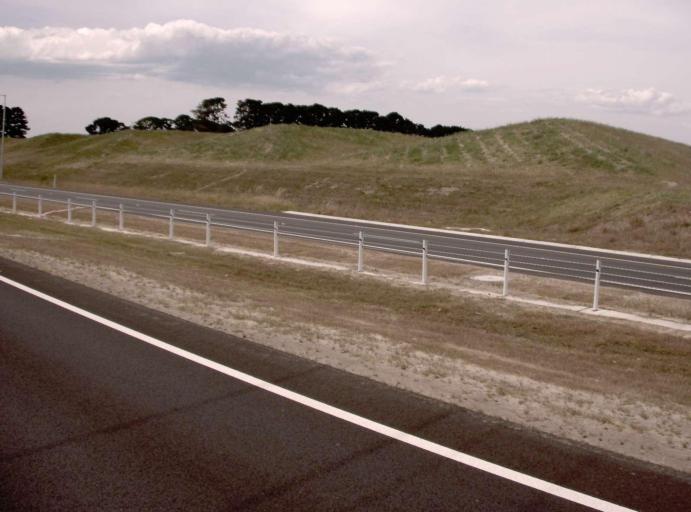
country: AU
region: Victoria
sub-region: Mornington Peninsula
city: Moorooduc
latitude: -38.2326
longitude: 145.1251
